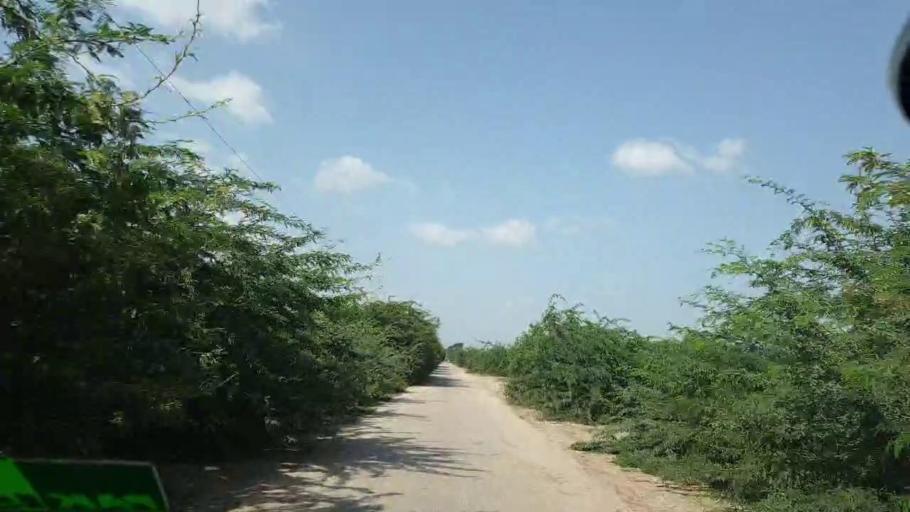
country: PK
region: Sindh
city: Kadhan
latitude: 24.6305
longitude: 69.2272
